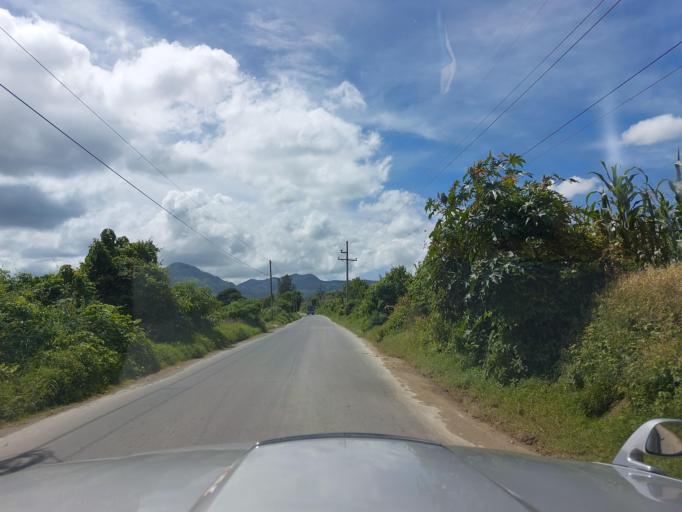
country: GT
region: Chimaltenango
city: Parramos
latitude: 14.6150
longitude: -90.8220
